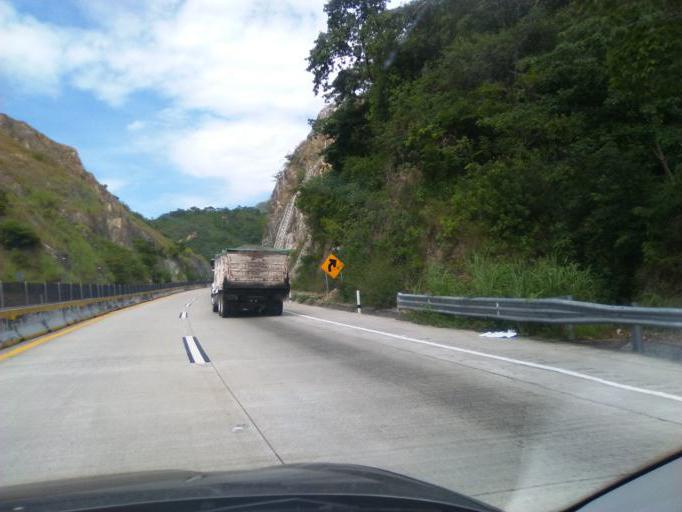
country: MX
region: Guerrero
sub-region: Chilpancingo de los Bravo
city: Julian Blanco (Dos Caminos)
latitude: 17.2057
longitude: -99.5379
